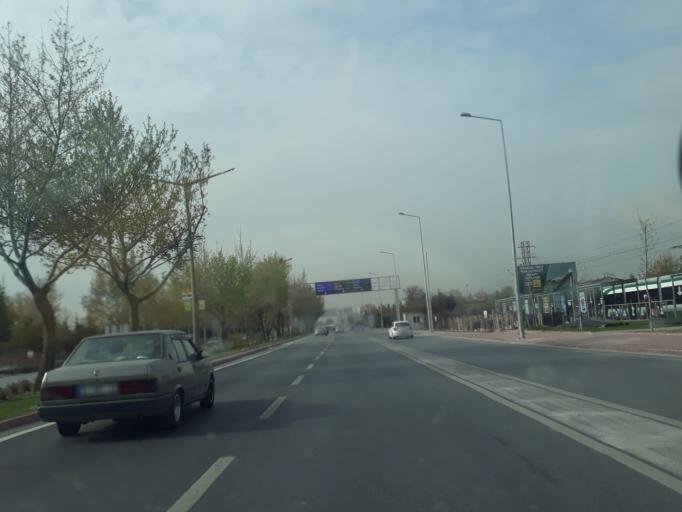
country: TR
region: Konya
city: Selcuklu
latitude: 37.9545
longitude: 32.5135
